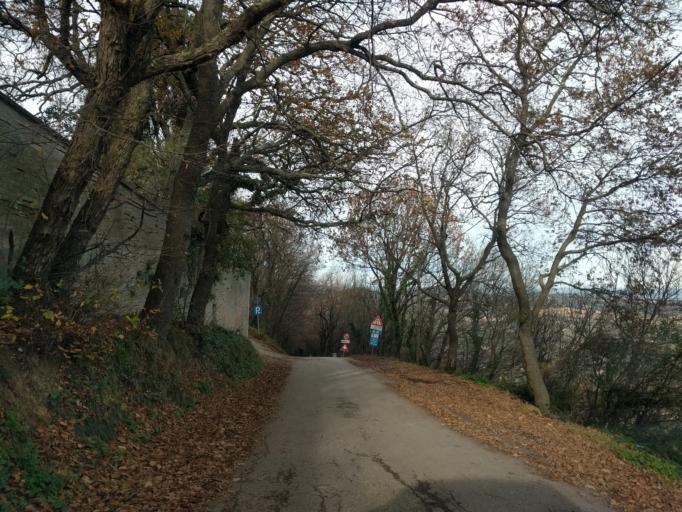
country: IT
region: The Marches
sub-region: Provincia di Pesaro e Urbino
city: Centinarola
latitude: 43.8190
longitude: 12.9754
